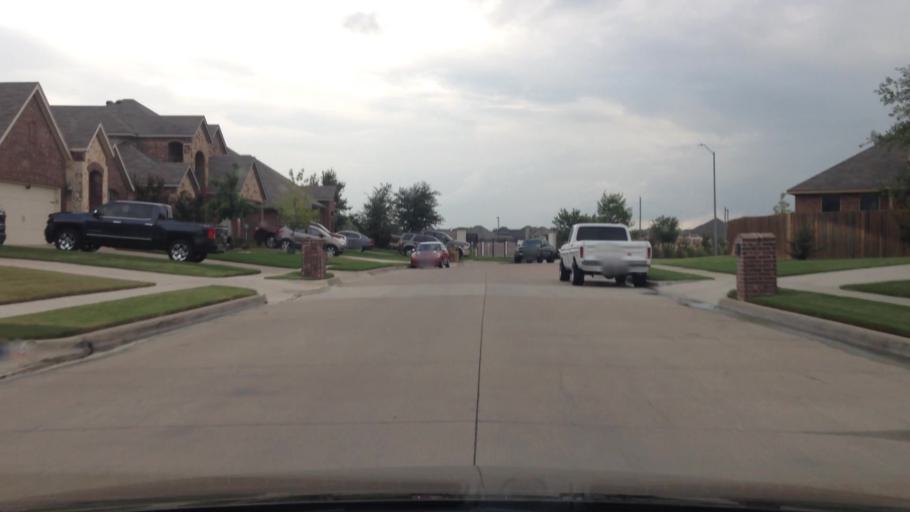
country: US
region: Texas
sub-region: Johnson County
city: Burleson
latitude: 32.5686
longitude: -97.3338
